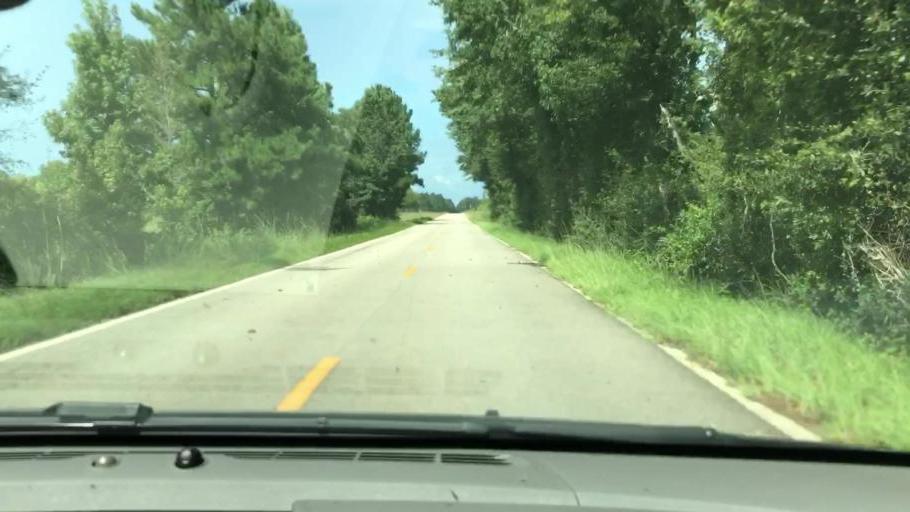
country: US
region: Georgia
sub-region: Seminole County
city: Donalsonville
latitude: 31.1371
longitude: -84.9952
